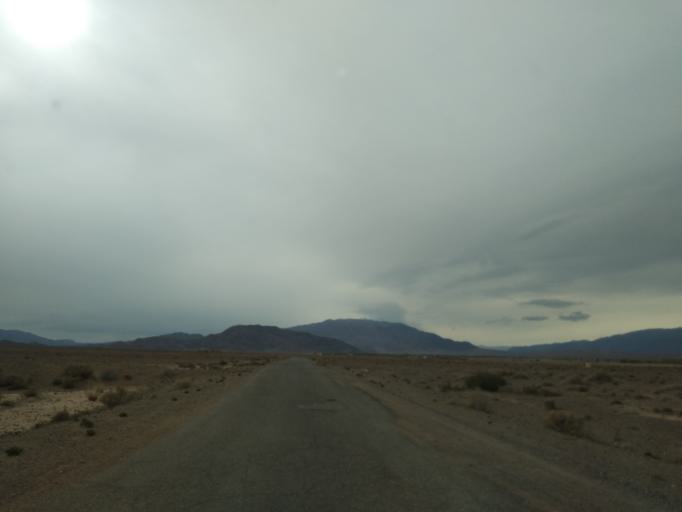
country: KG
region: Ysyk-Koel
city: Balykchy
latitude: 42.3193
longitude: 76.2292
